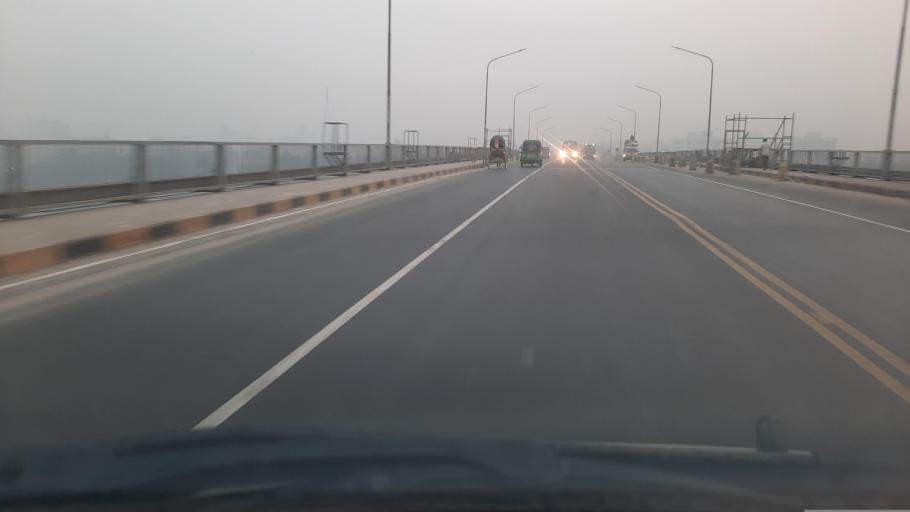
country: BD
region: Dhaka
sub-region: Dhaka
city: Dhaka
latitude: 23.6864
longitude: 90.4260
